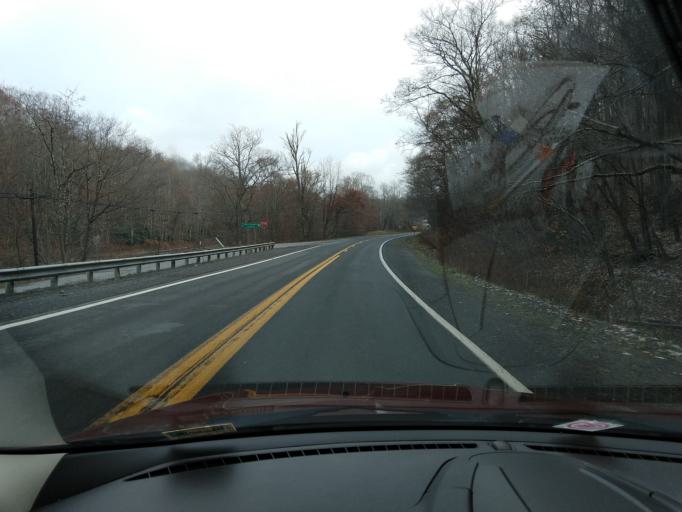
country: US
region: West Virginia
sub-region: Greenbrier County
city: Rainelle
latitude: 38.0398
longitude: -80.7292
